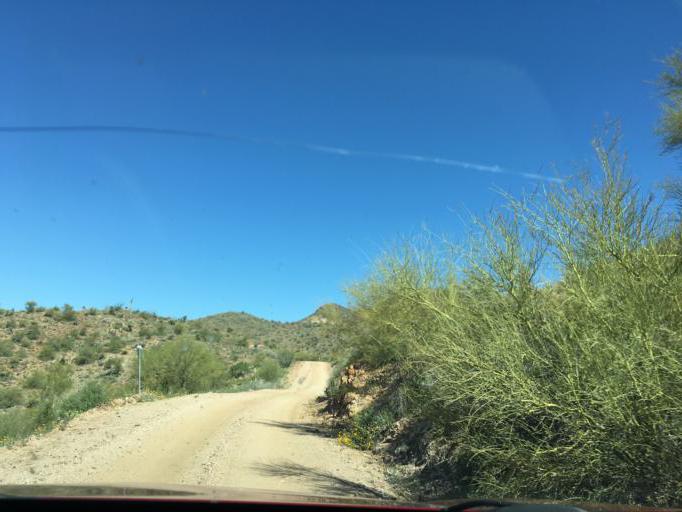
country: US
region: Arizona
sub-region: Yavapai County
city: Bagdad
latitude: 34.6068
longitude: -113.3981
